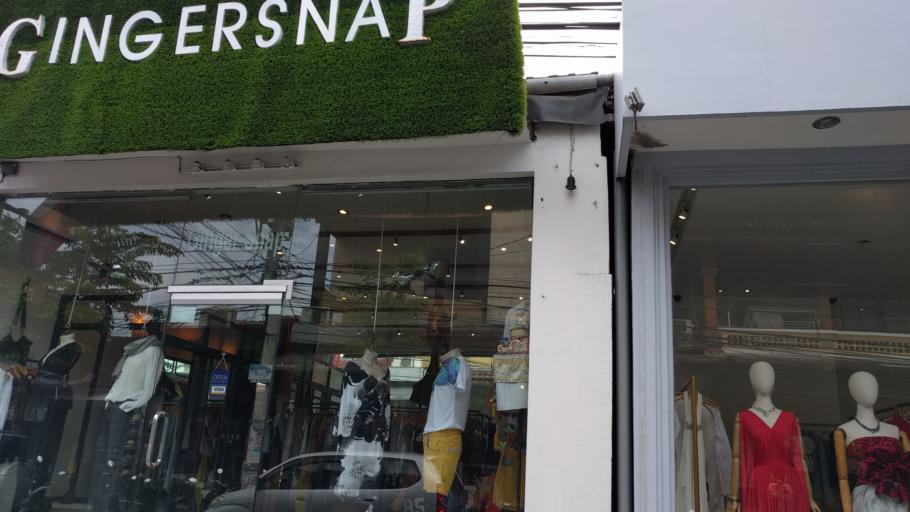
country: ID
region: Bali
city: Kuta
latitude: -8.6901
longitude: 115.1676
